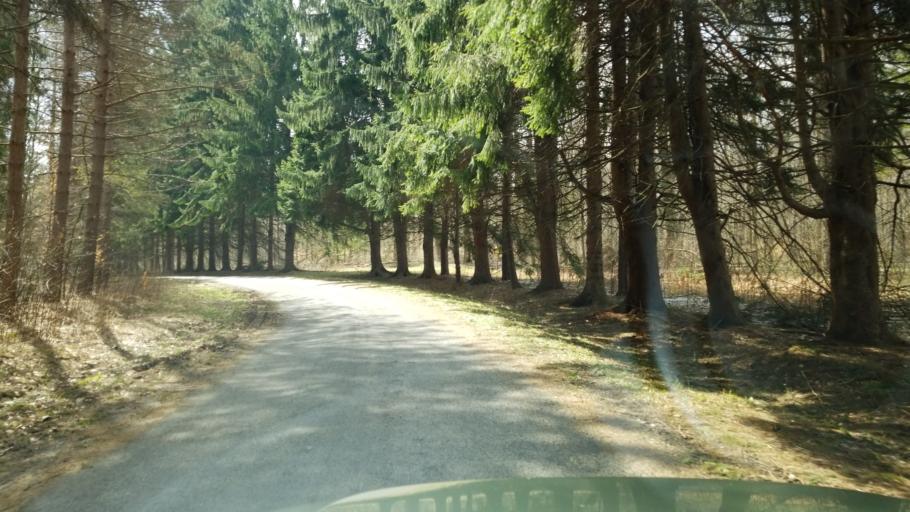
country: US
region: Pennsylvania
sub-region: Jefferson County
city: Brockway
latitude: 41.2864
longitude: -78.8758
